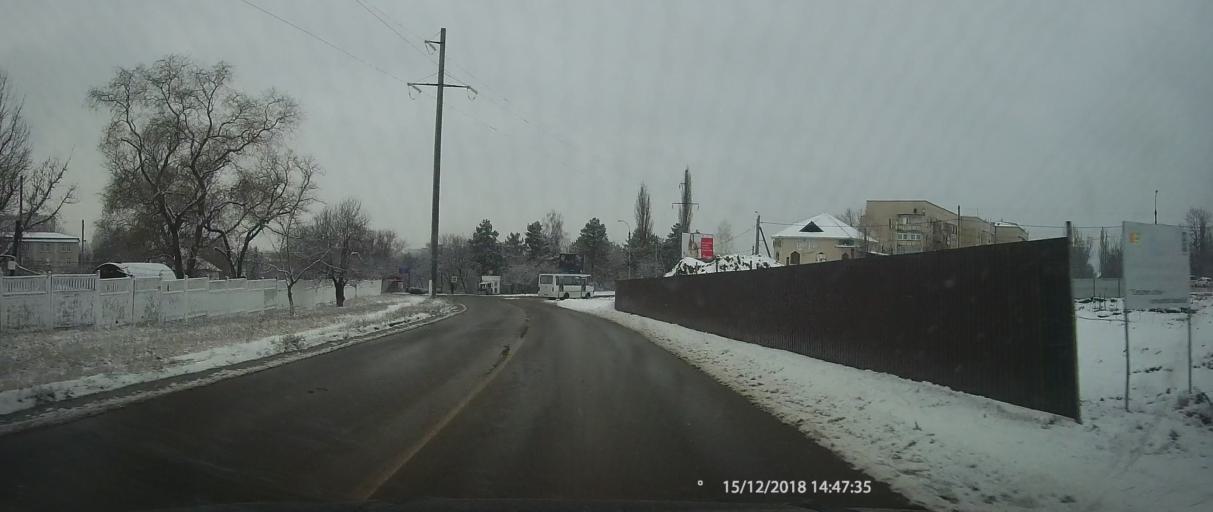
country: MD
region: Cahul
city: Cahul
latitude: 45.8950
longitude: 28.2050
